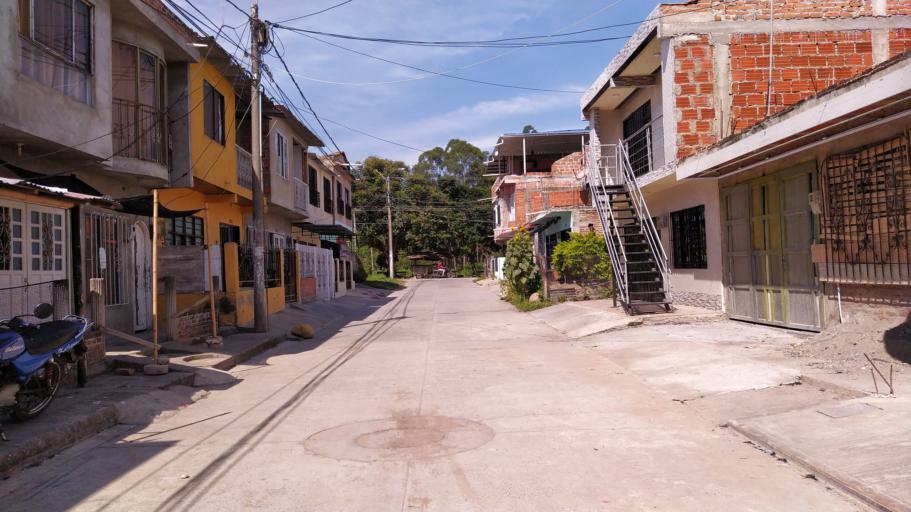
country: CO
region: Valle del Cauca
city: Florida
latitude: 3.3193
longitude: -76.2230
